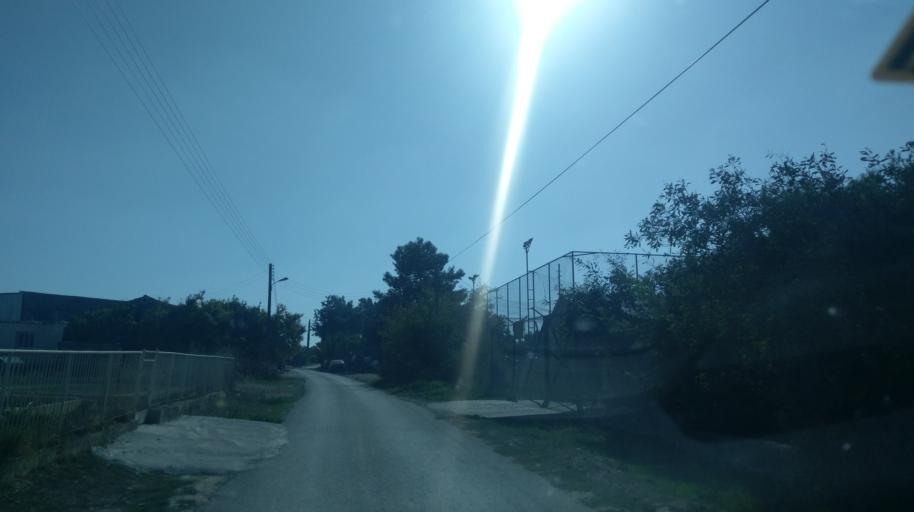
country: CY
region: Lefkosia
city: Lympia
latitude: 35.0081
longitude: 33.4642
